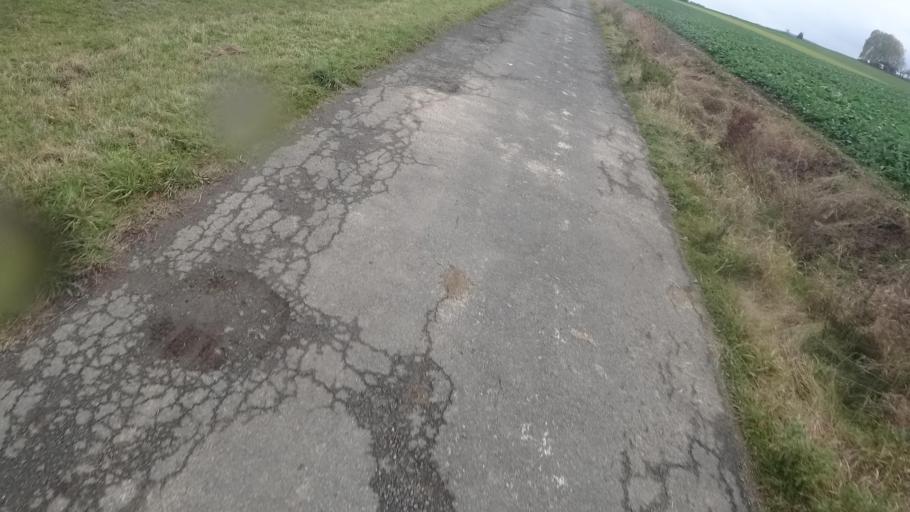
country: DE
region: Rheinland-Pfalz
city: Prath
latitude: 50.1623
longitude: 7.6807
